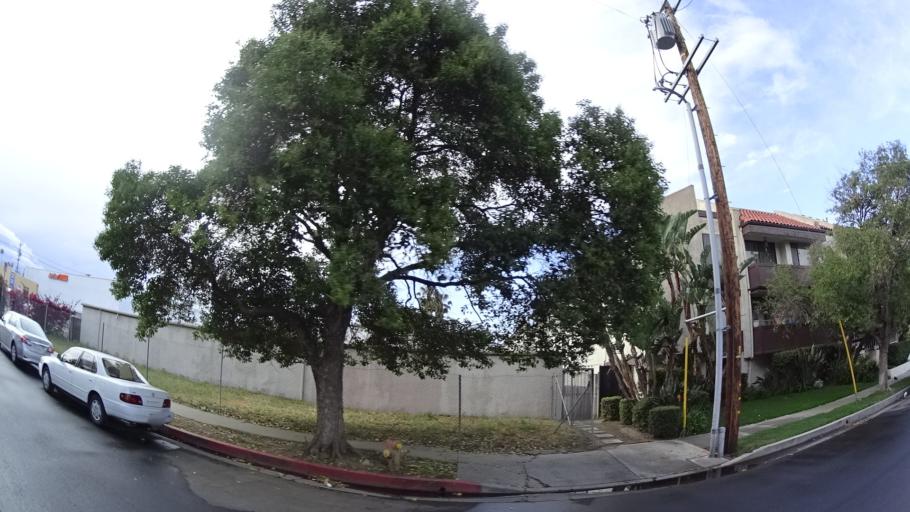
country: US
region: California
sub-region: Los Angeles County
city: Sherman Oaks
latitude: 34.1640
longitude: -118.4475
